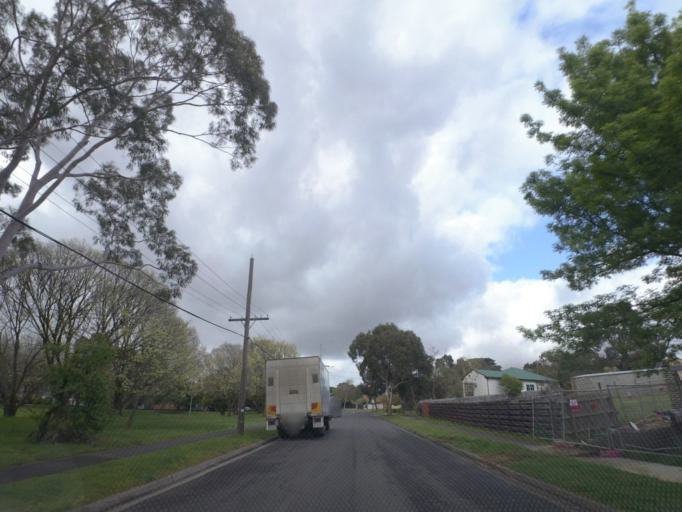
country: AU
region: Victoria
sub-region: Whitehorse
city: Blackburn
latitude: -37.8166
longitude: 145.1449
